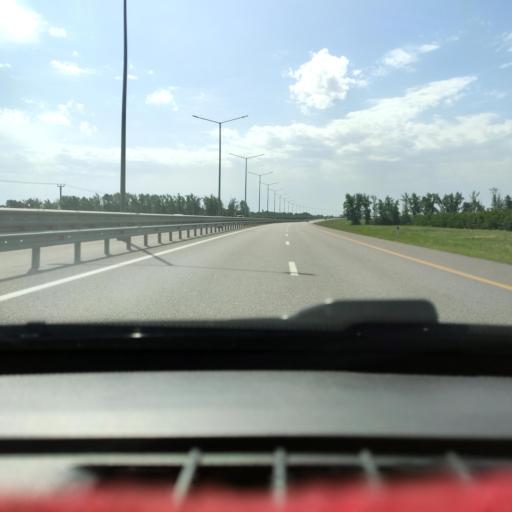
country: RU
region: Voronezj
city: Podkletnoye
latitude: 51.5813
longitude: 39.4603
